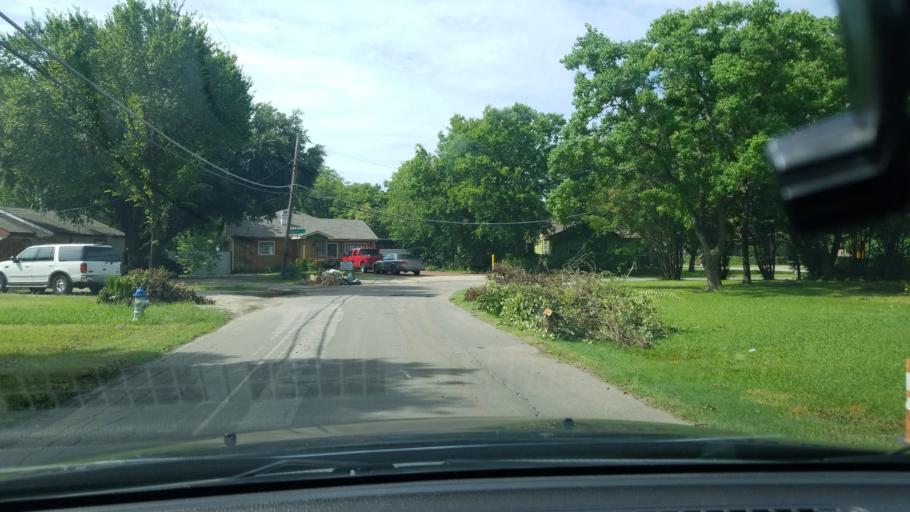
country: US
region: Texas
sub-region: Dallas County
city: Balch Springs
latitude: 32.7673
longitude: -96.6771
